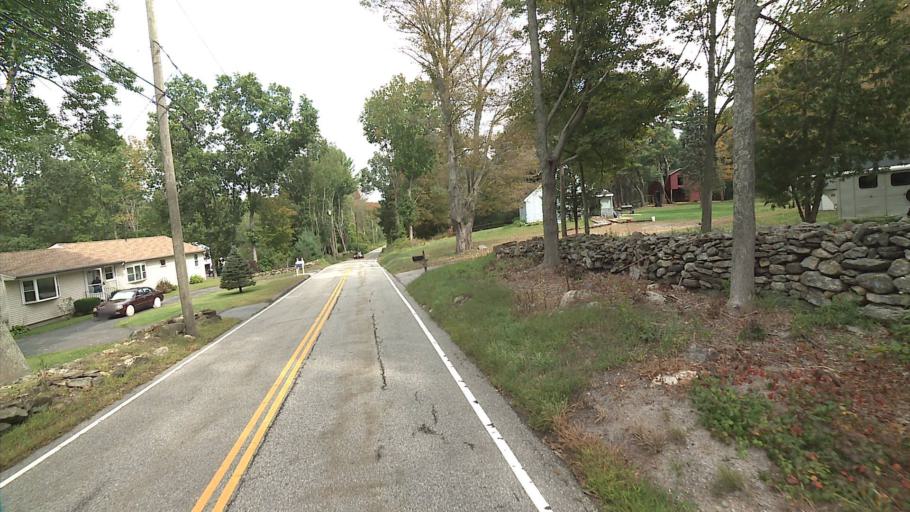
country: US
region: Connecticut
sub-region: Tolland County
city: Stafford Springs
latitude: 41.8946
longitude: -72.2680
